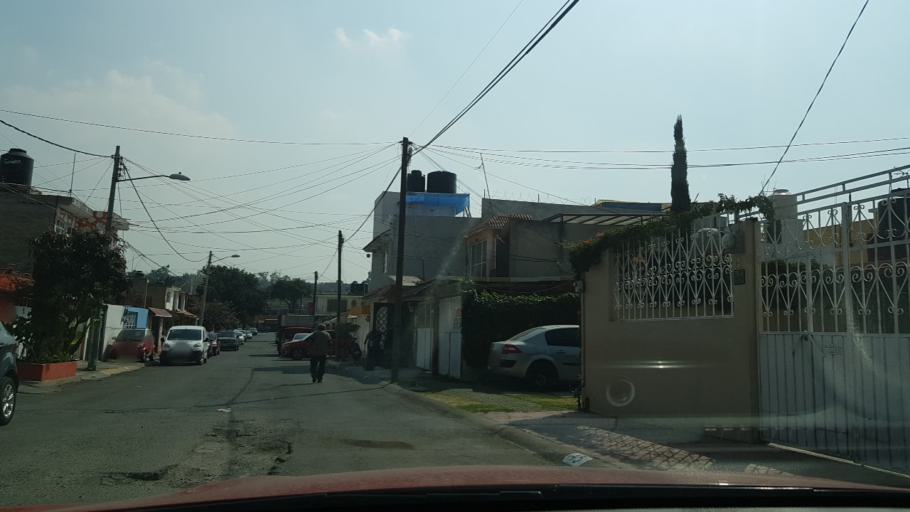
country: MX
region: Mexico
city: Cuautitlan Izcalli
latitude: 19.6446
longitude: -99.2122
